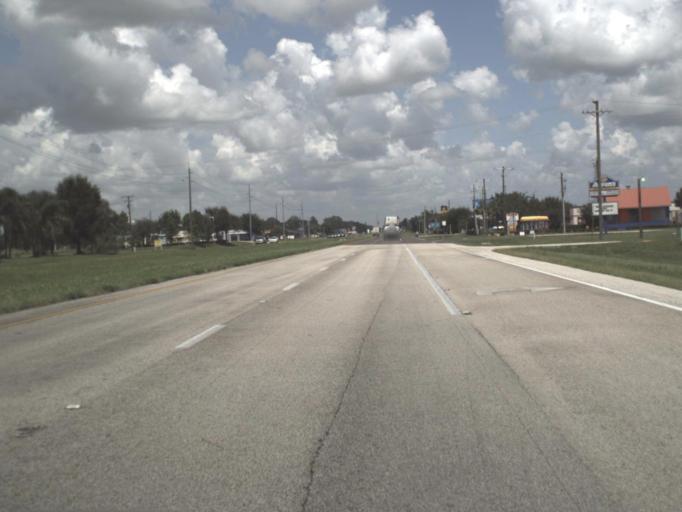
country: US
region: Florida
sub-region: Hardee County
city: Wauchula
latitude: 27.5650
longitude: -81.8147
